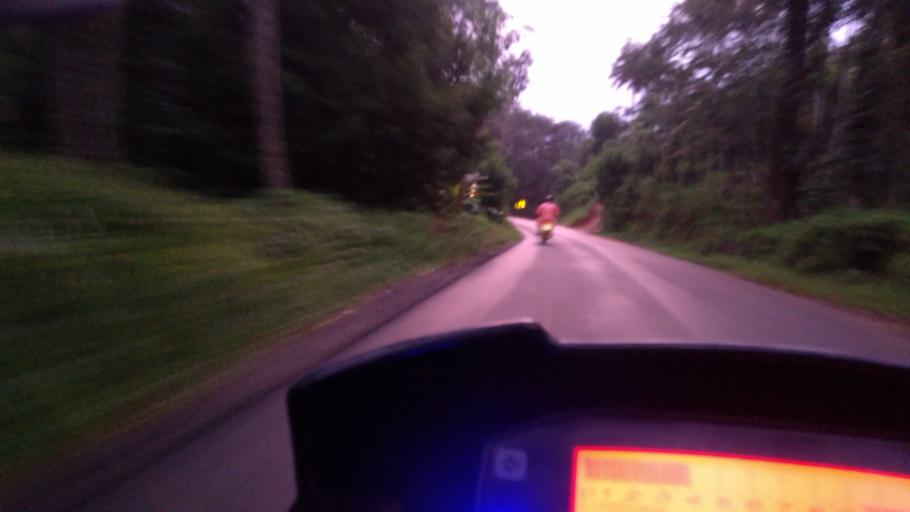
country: IN
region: Kerala
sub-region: Idukki
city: Munnar
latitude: 9.9638
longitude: 77.0698
